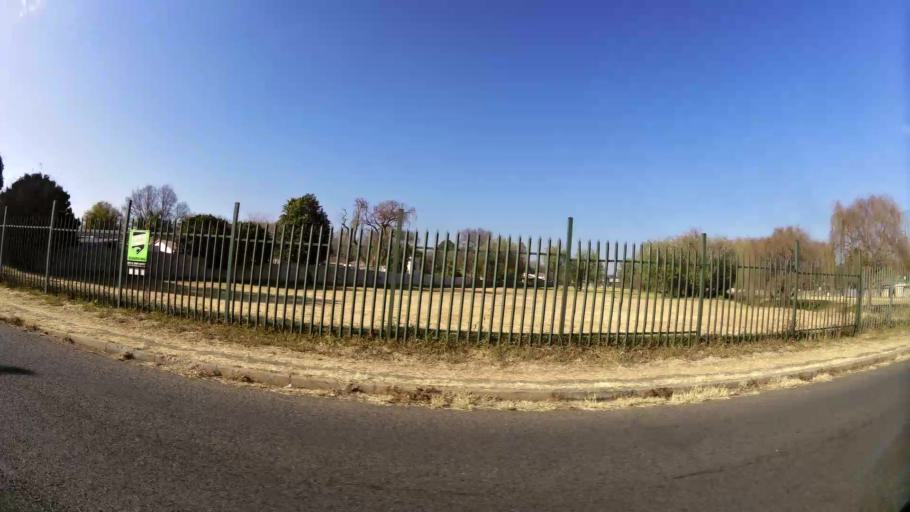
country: ZA
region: Gauteng
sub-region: City of Johannesburg Metropolitan Municipality
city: Modderfontein
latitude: -26.1454
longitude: 28.1670
